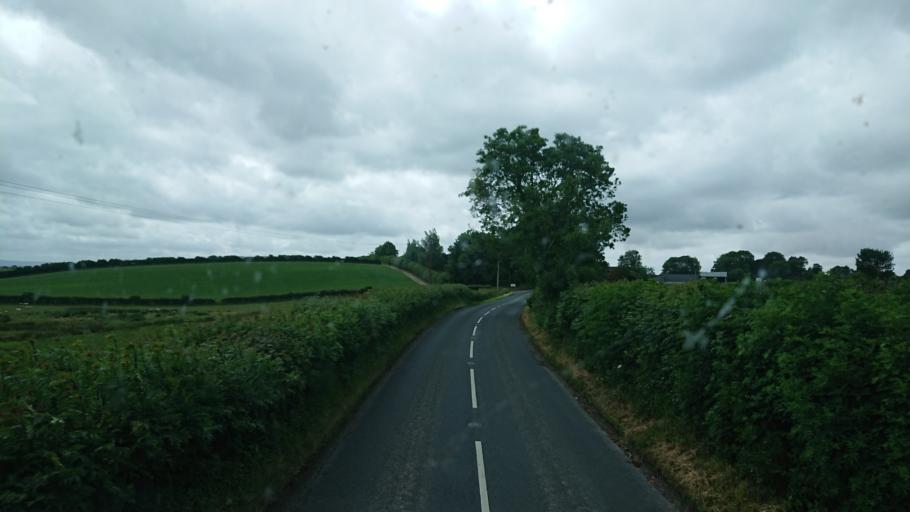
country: GB
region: England
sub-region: Cumbria
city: Milnthorpe
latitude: 54.2316
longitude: -2.7434
